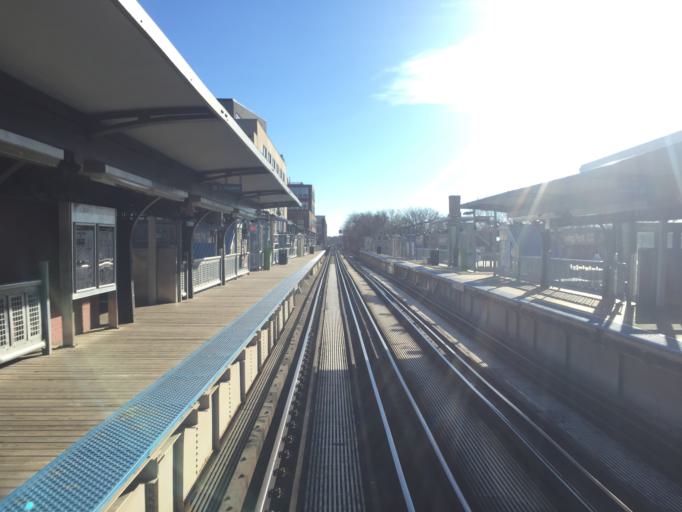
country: US
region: Illinois
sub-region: Cook County
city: Lincolnwood
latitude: 41.9544
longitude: -87.6750
